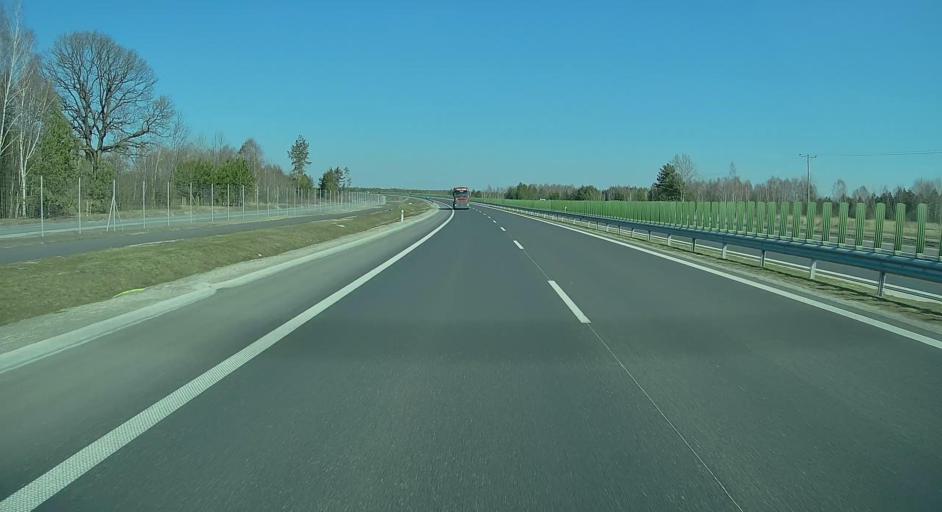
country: PL
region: Subcarpathian Voivodeship
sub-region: Powiat nizanski
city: Konczyce
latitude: 50.4333
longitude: 22.1363
